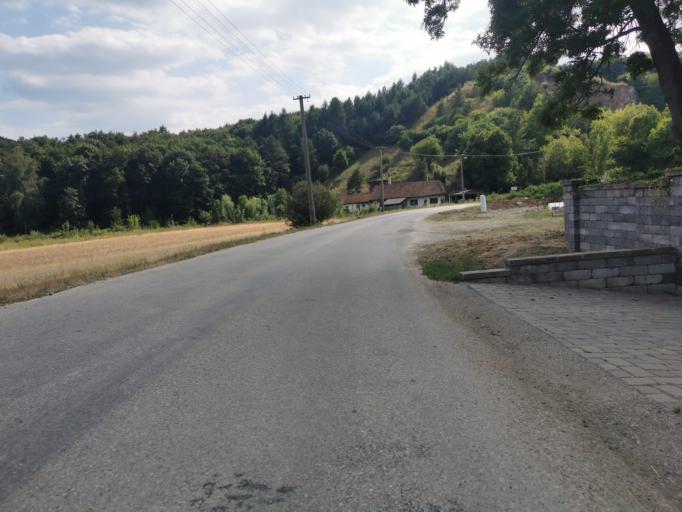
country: SK
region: Trenciansky
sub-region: Okres Myjava
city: Myjava
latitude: 48.7481
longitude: 17.5257
